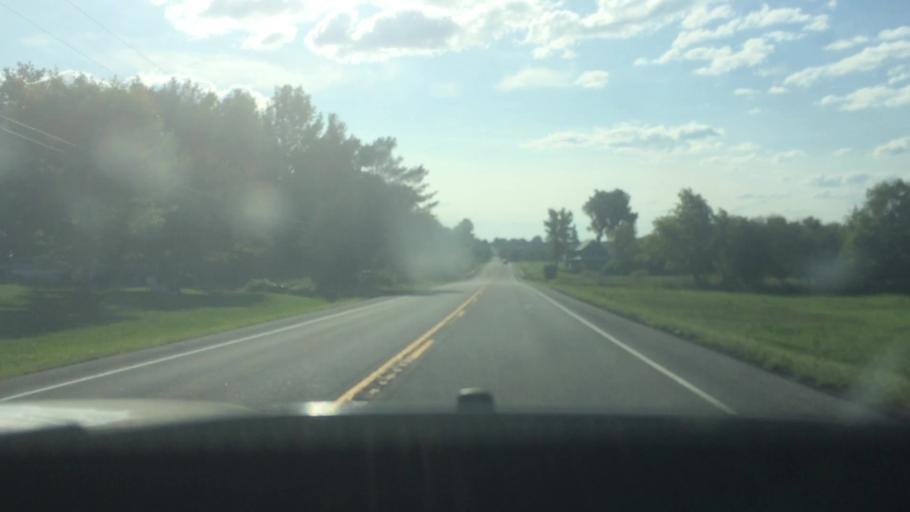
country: US
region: New York
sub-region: St. Lawrence County
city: Potsdam
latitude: 44.6892
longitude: -74.7241
